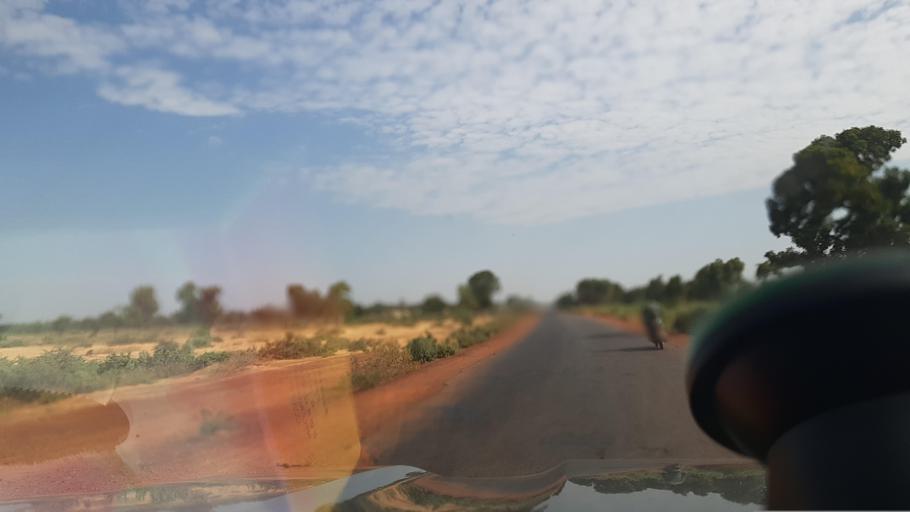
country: ML
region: Segou
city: Segou
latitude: 13.5021
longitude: -6.1497
